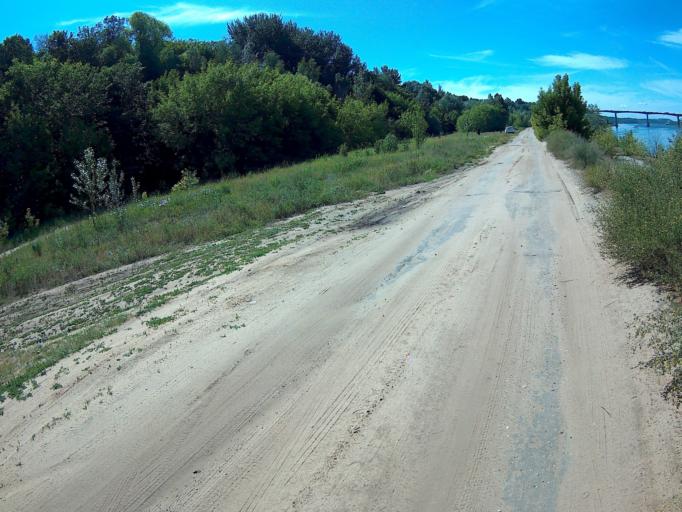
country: RU
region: Nizjnij Novgorod
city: Nizhniy Novgorod
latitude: 56.2594
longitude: 43.9662
